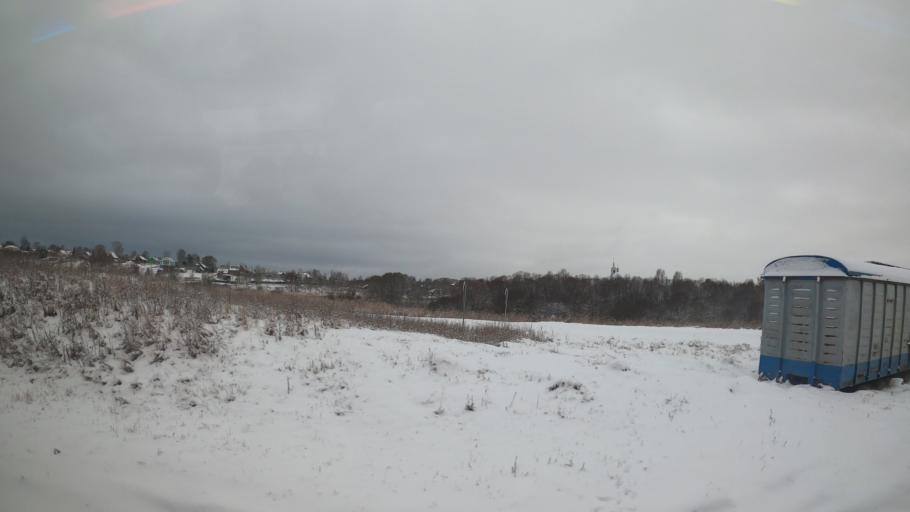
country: RU
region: Jaroslavl
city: Pereslavl'-Zalesskiy
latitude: 56.7041
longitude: 38.9097
